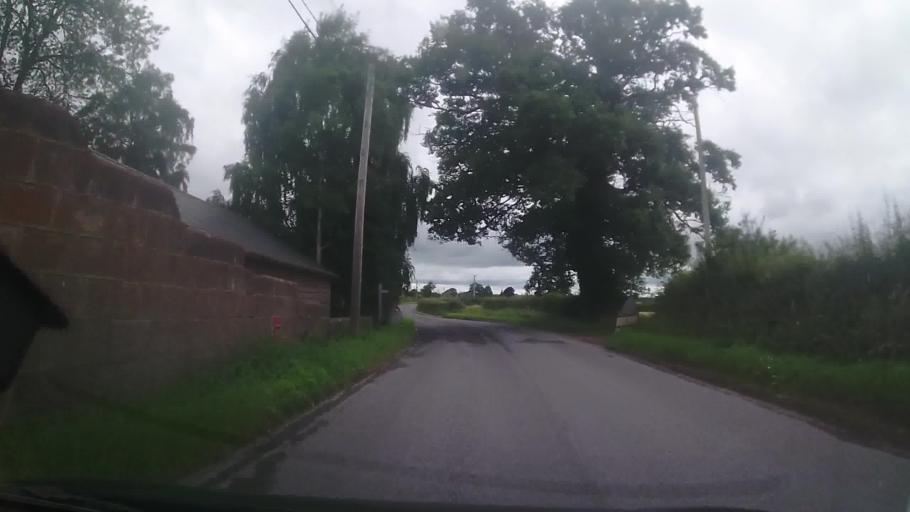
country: GB
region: England
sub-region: Shropshire
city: Petton
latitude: 52.8404
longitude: -2.8230
